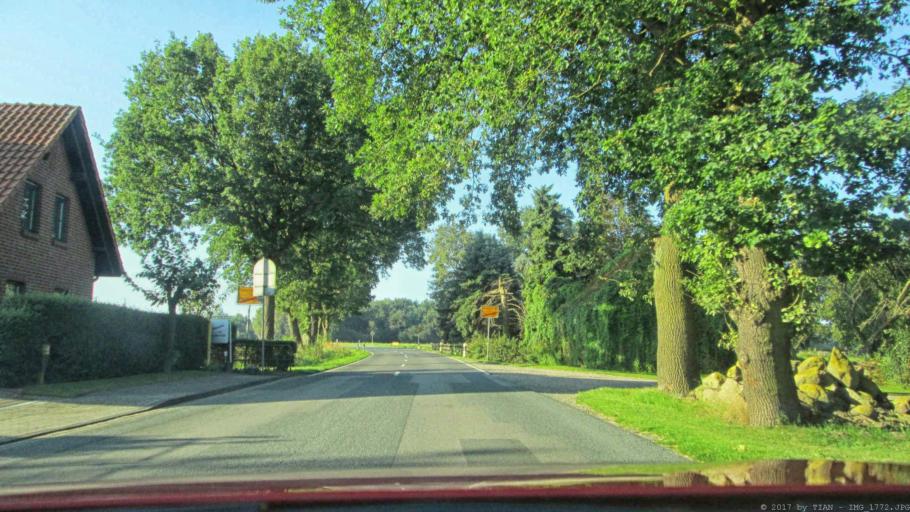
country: DE
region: Lower Saxony
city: Tiddische
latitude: 52.4984
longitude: 10.8008
